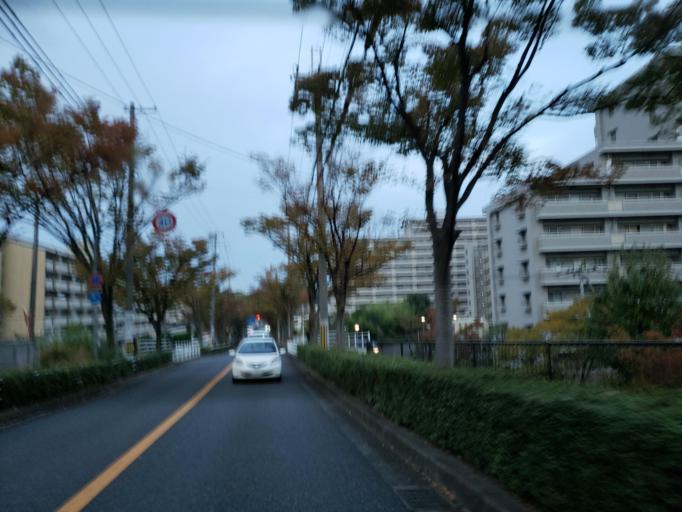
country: JP
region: Osaka
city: Suita
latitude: 34.7931
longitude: 135.5280
